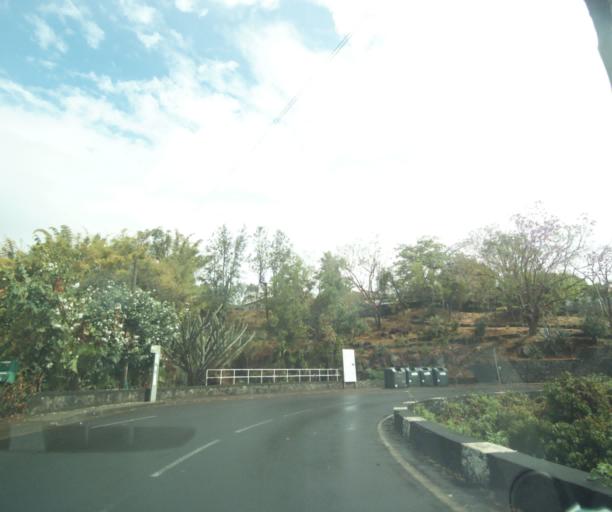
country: RE
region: Reunion
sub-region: Reunion
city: Saint-Paul
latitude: -20.9993
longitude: 55.3260
